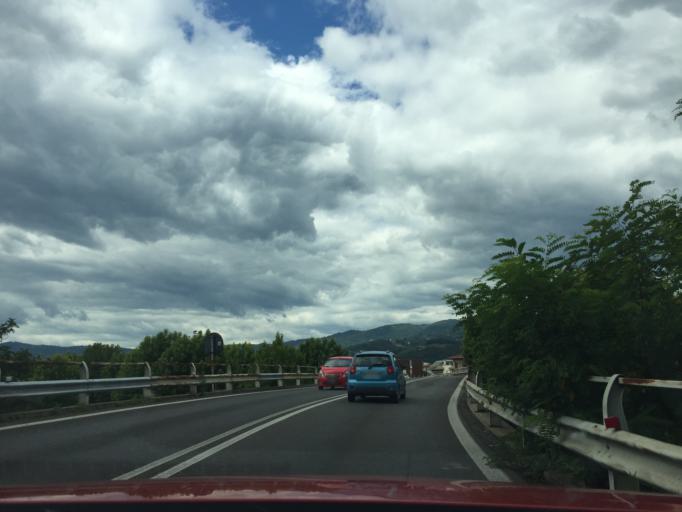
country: IT
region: Tuscany
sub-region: Provincia di Pistoia
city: Pieve a Nievole
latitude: 43.8776
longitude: 10.7870
